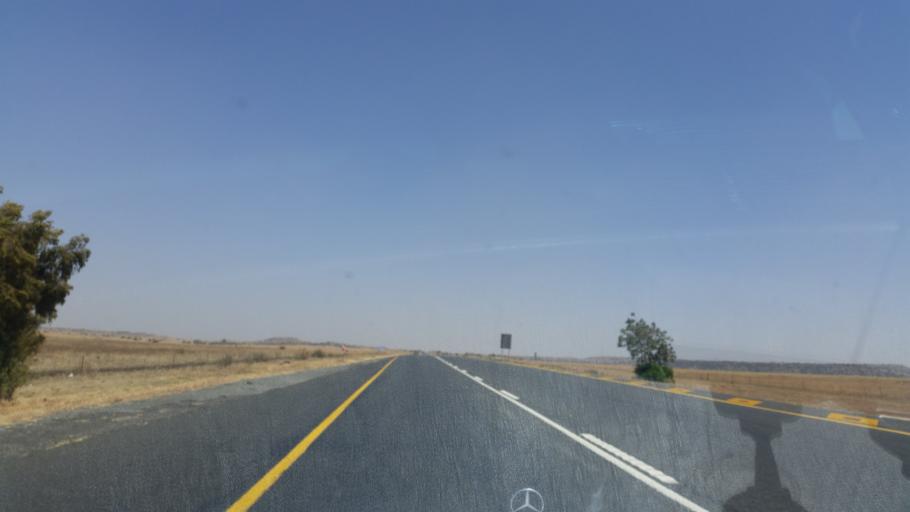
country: ZA
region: Orange Free State
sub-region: Lejweleputswa District Municipality
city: Winburg
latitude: -28.6802
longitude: 26.8305
